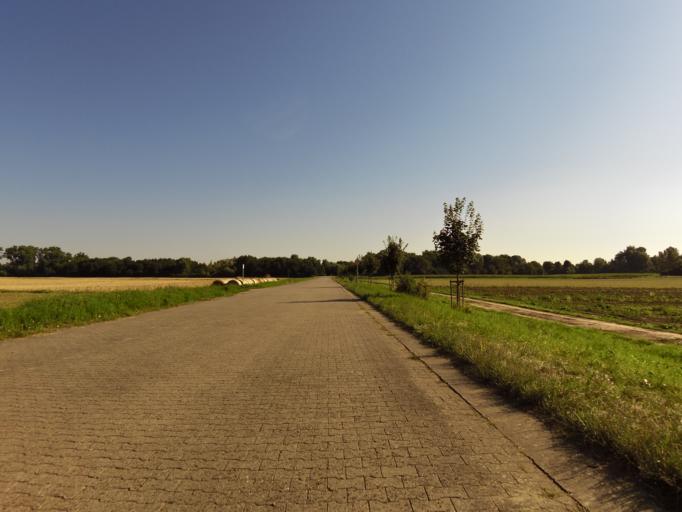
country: DE
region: Hesse
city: Gernsheim
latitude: 49.7441
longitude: 8.4736
